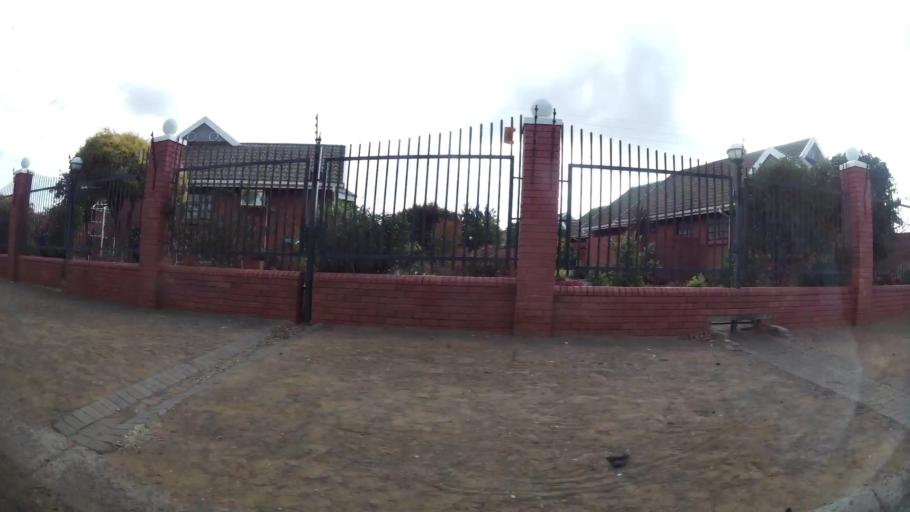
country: ZA
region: Orange Free State
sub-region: Mangaung Metropolitan Municipality
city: Bloemfontein
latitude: -29.0768
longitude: 26.1987
